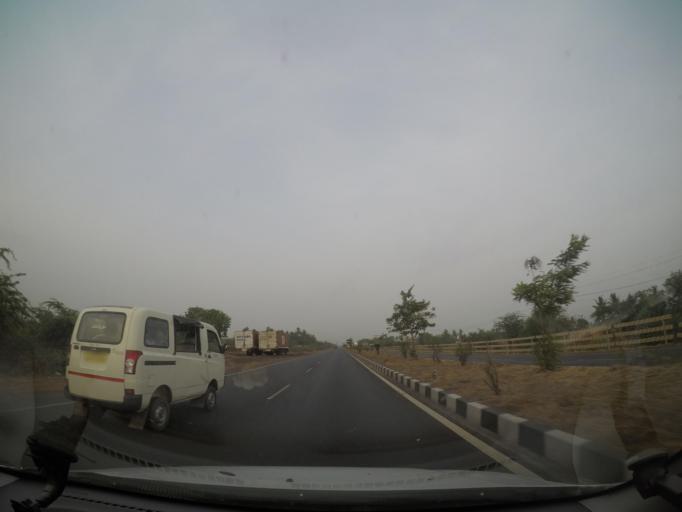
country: IN
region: Andhra Pradesh
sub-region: Krishna
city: Gannavaram
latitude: 16.6261
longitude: 80.9398
